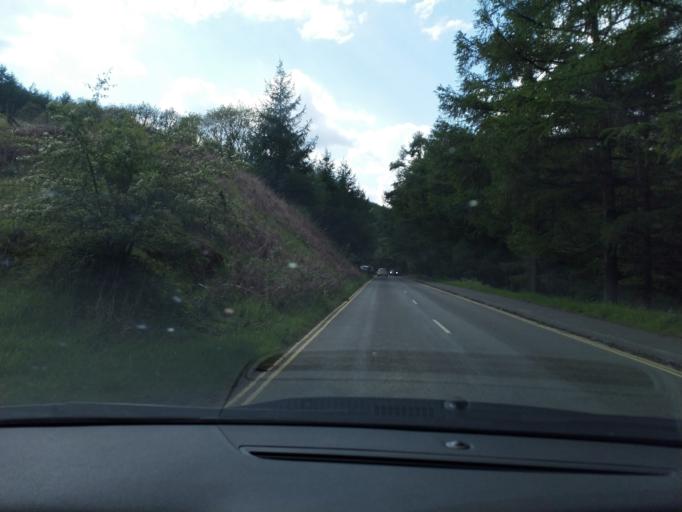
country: GB
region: England
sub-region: Derbyshire
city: Hope Valley
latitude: 53.3933
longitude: -1.7318
